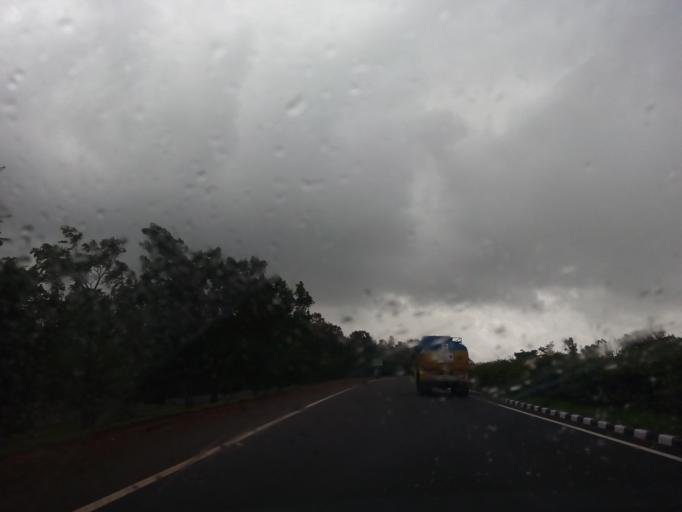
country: IN
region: Karnataka
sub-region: Belgaum
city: Belgaum
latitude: 16.0124
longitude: 74.5165
